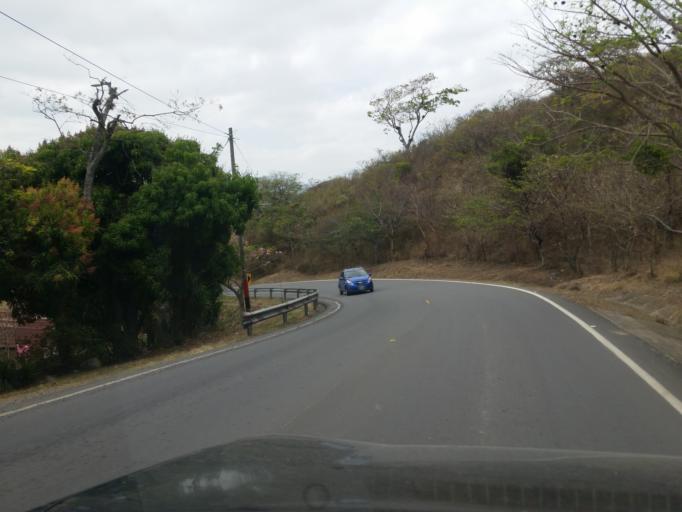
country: NI
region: Matagalpa
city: Matagalpa
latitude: 12.9526
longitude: -85.9196
